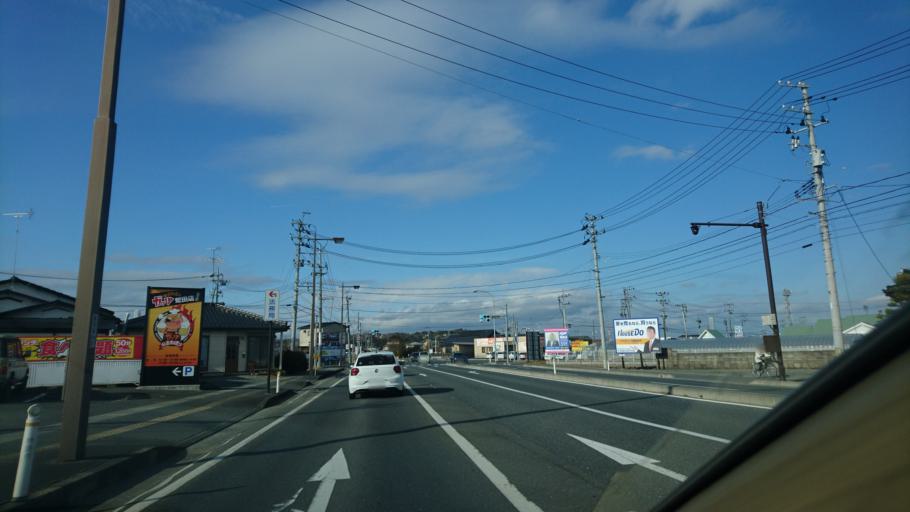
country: JP
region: Miyagi
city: Ishinomaki
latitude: 38.4518
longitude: 141.2655
